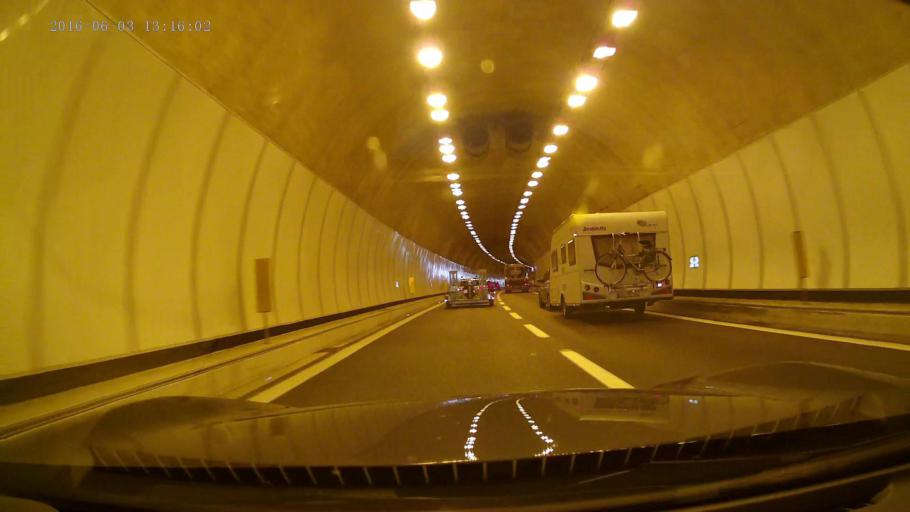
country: IT
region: Trentino-Alto Adige
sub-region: Bolzano
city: Ponte Gardena
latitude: 46.5960
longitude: 11.5328
